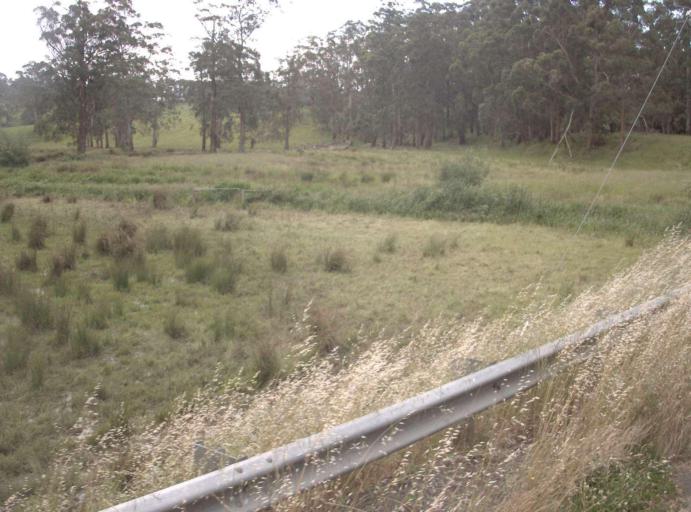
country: AU
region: Victoria
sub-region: Baw Baw
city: Warragul
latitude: -38.0840
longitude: 145.9207
